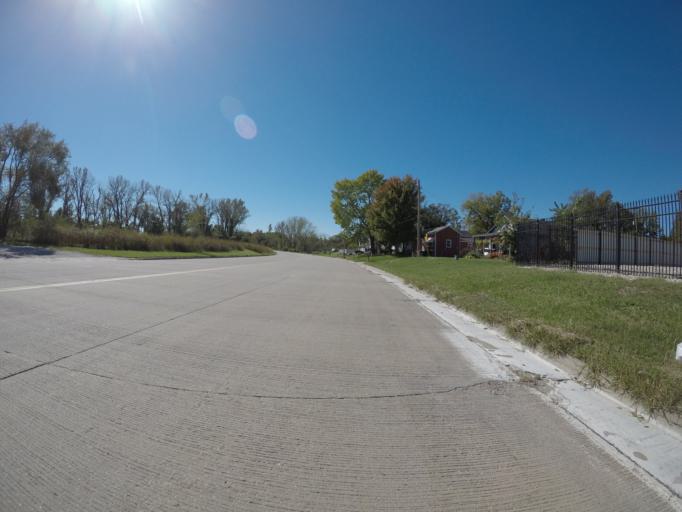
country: US
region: Kansas
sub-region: Wyandotte County
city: Bonner Springs
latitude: 39.0503
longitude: -94.8890
